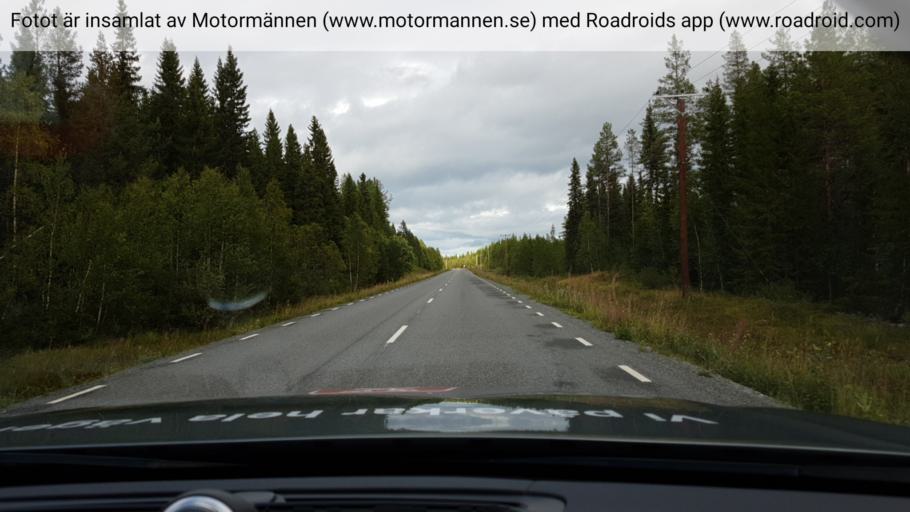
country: SE
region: Jaemtland
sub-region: Krokoms Kommun
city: Krokom
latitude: 63.6444
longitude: 14.4355
